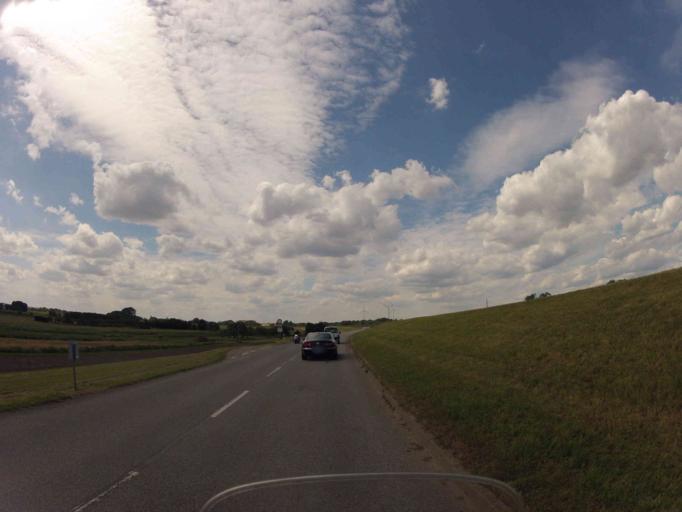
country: DE
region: Hamburg
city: Rothenburgsort
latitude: 53.4988
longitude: 10.0669
